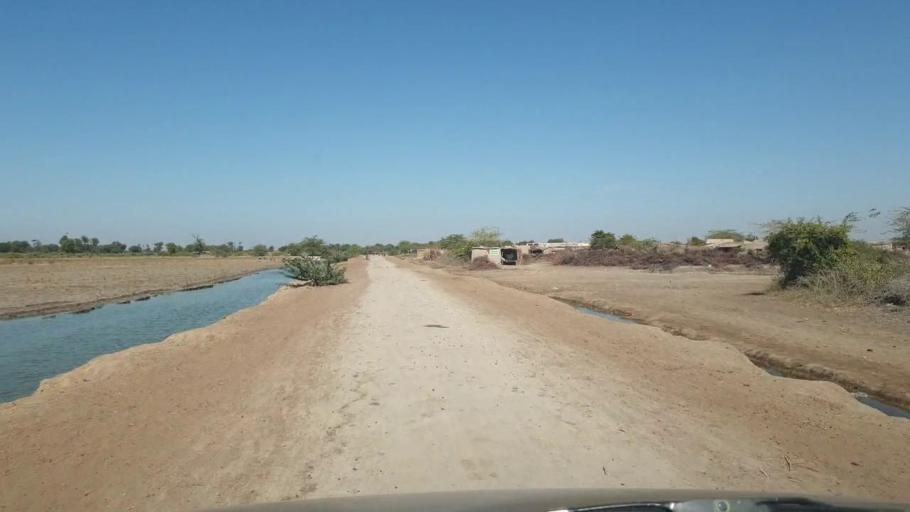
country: PK
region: Sindh
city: Umarkot
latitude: 25.4194
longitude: 69.6452
